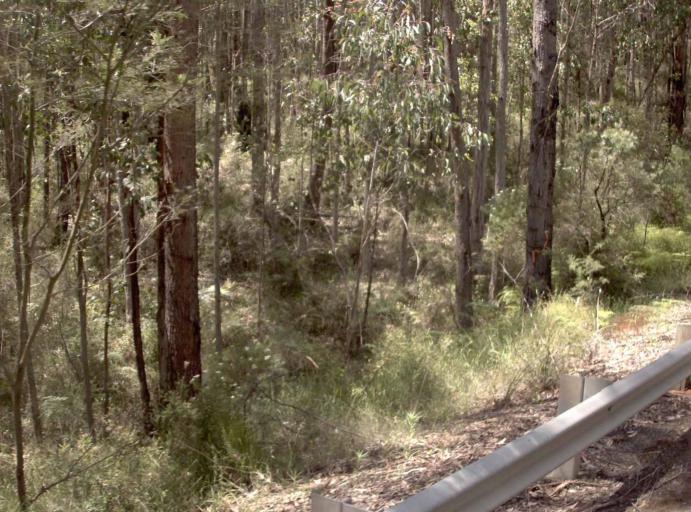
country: AU
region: New South Wales
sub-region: Bombala
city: Bombala
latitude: -37.5690
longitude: 149.3197
